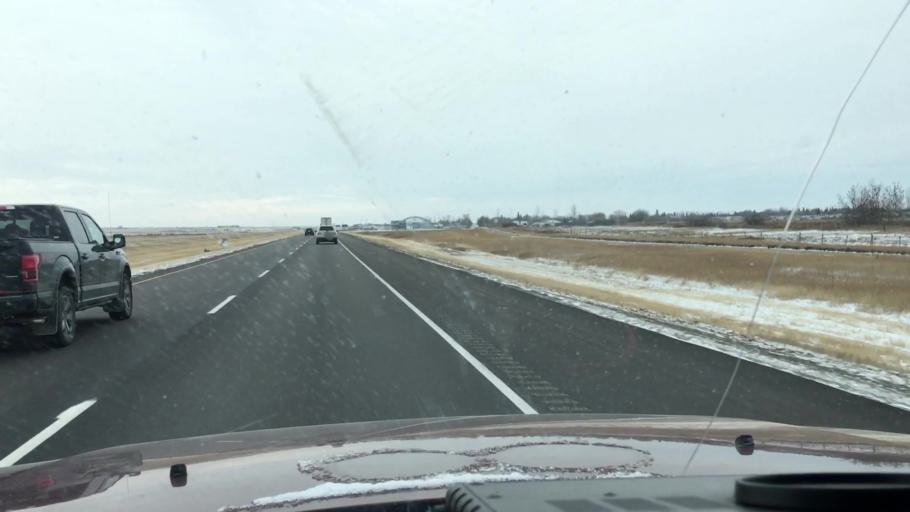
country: CA
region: Saskatchewan
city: Saskatoon
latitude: 51.8226
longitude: -106.5000
